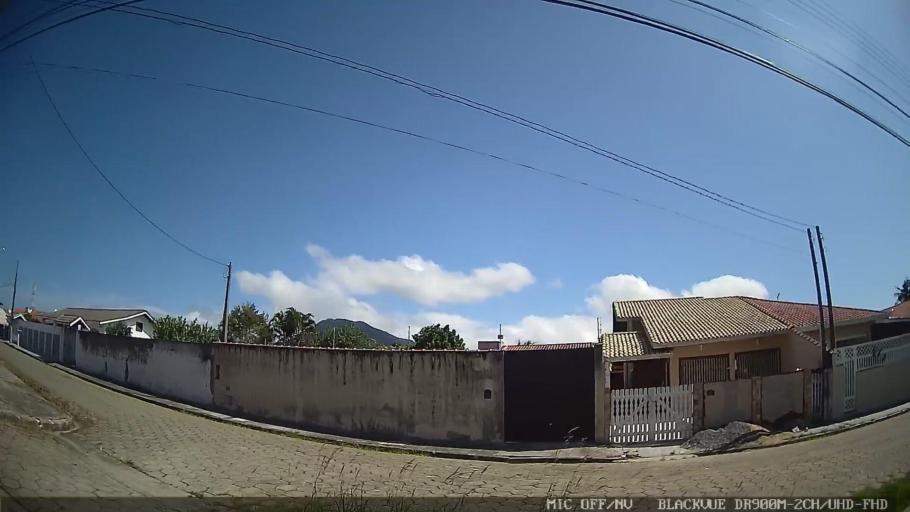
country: BR
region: Sao Paulo
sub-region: Peruibe
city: Peruibe
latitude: -24.3125
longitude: -46.9951
